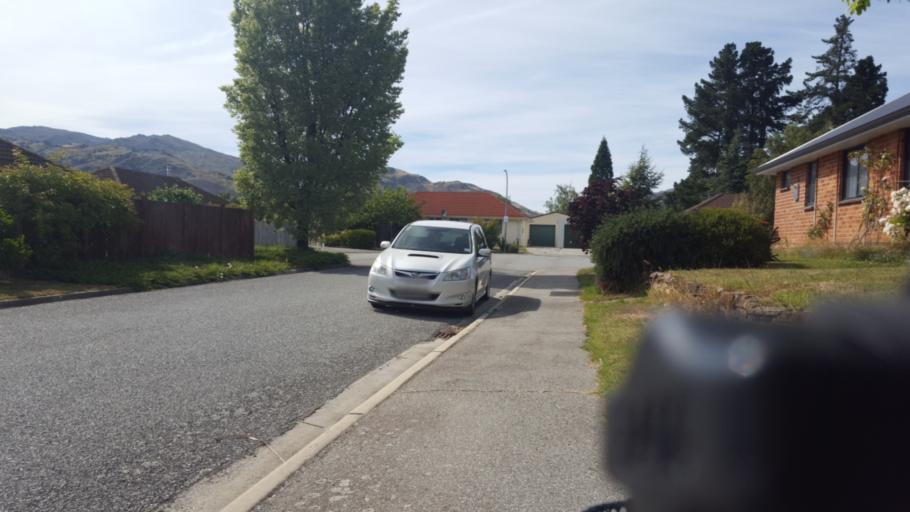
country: NZ
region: Otago
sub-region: Queenstown-Lakes District
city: Wanaka
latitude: -45.0417
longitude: 169.1911
